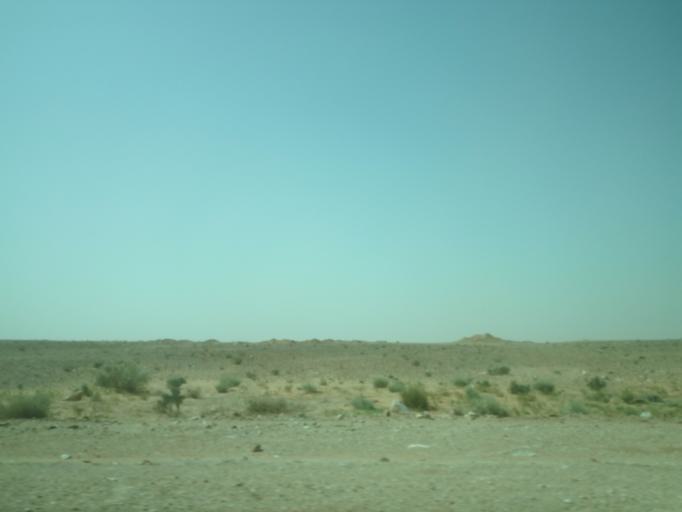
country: DZ
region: Ghardaia
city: Berriane
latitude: 32.8159
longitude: 4.1422
